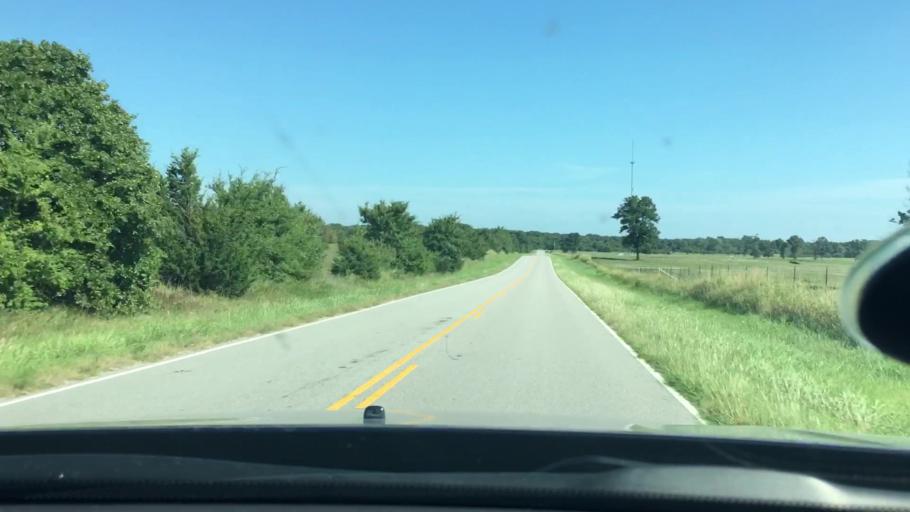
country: US
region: Oklahoma
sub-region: Johnston County
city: Tishomingo
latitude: 34.3533
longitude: -96.5488
